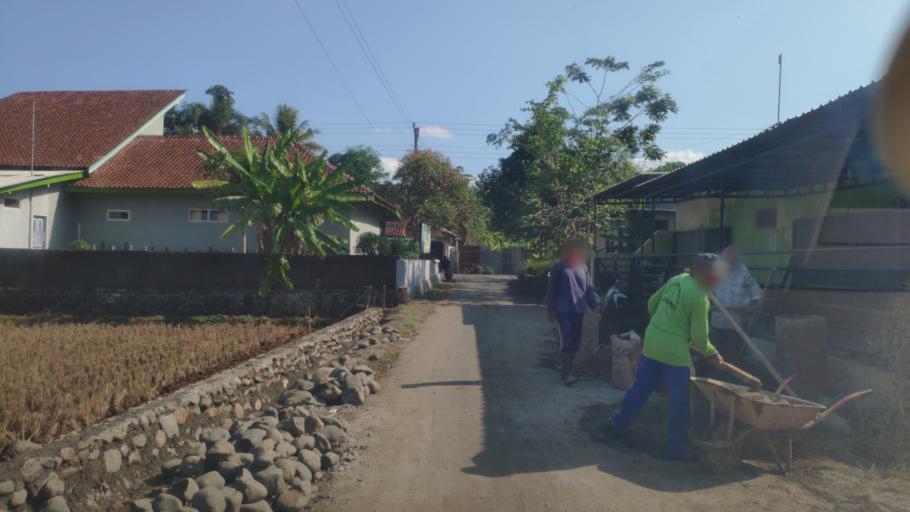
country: ID
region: Central Java
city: Purbalingga
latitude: -7.4768
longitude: 109.4483
